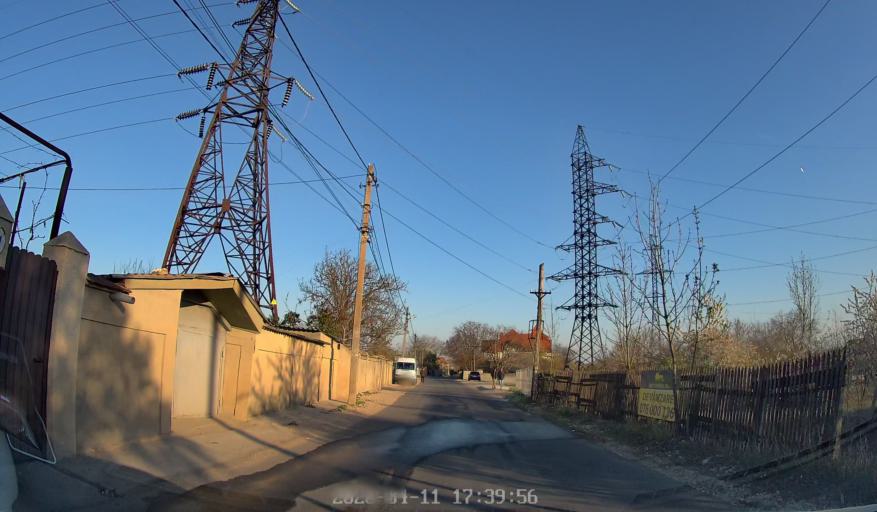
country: MD
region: Laloveni
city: Ialoveni
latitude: 46.9815
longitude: 28.8084
